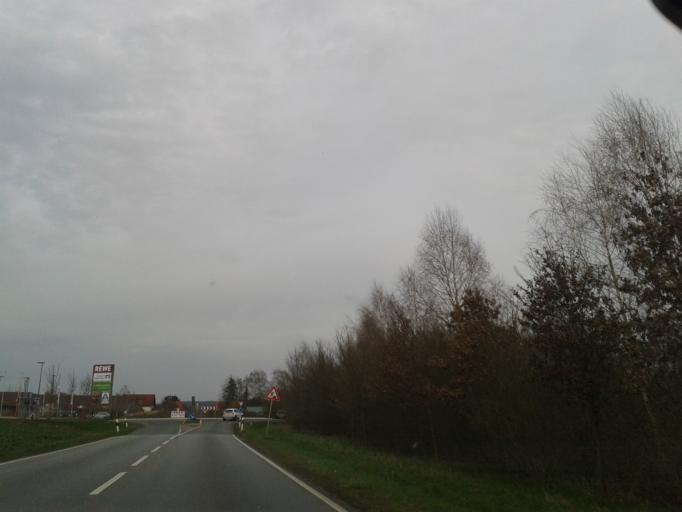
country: DE
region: Hesse
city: Wetter
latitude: 50.8584
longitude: 8.6943
